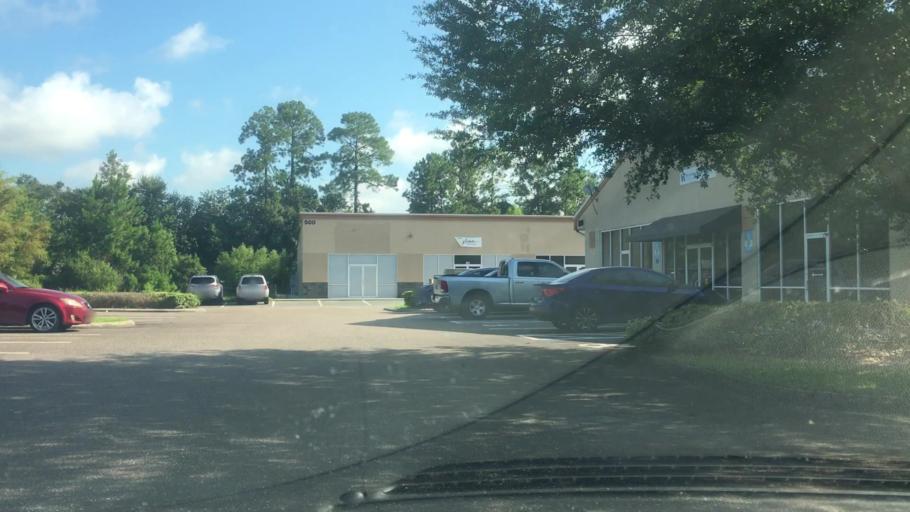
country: US
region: Florida
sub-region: Duval County
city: Jacksonville
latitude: 30.4398
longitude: -81.6827
